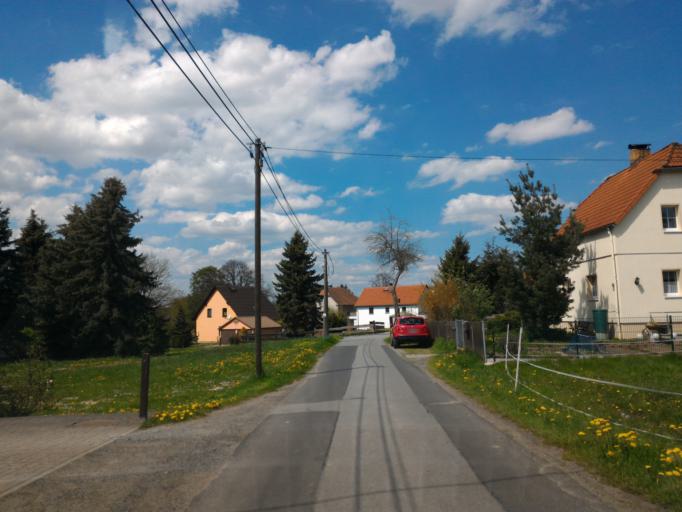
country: DE
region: Saxony
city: Leutersdorf
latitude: 50.9518
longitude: 14.6654
